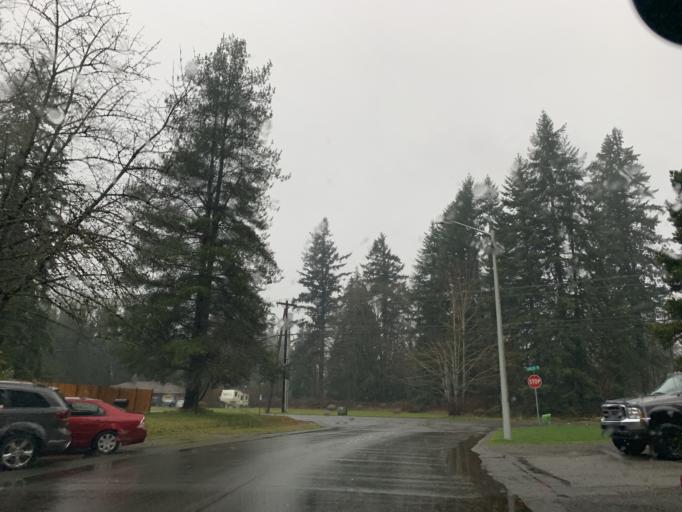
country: US
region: Washington
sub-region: Snohomish County
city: Marysville
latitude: 48.0889
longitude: -122.1662
